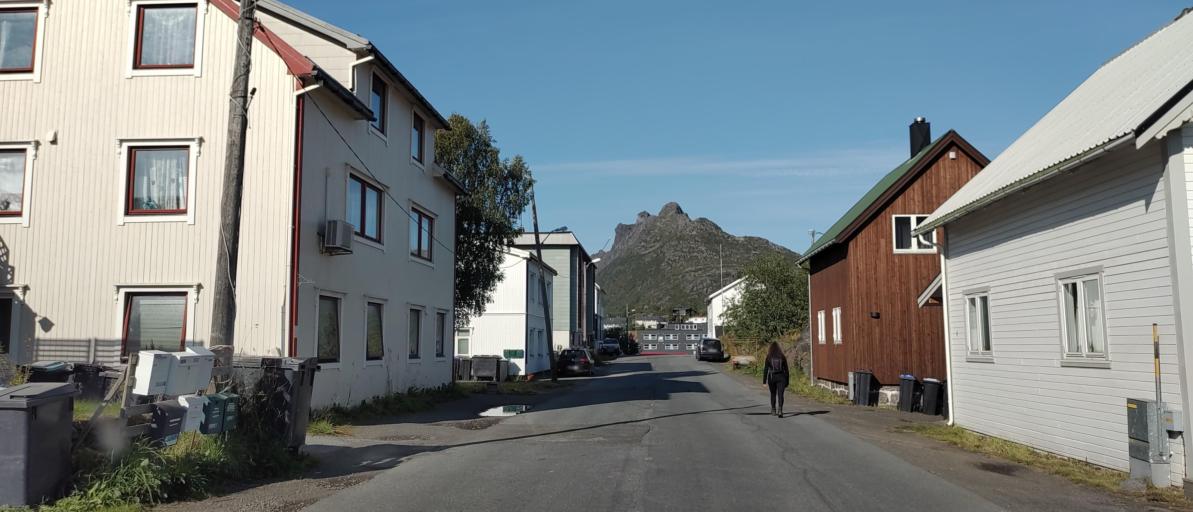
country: NO
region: Nordland
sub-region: Vagan
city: Svolvaer
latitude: 68.2383
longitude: 14.5705
